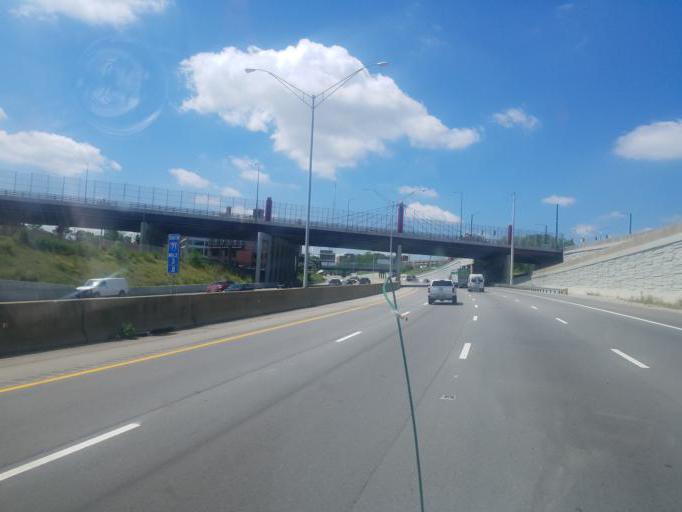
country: US
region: Kentucky
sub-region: Campbell County
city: Dayton
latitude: 39.1358
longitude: -84.4923
